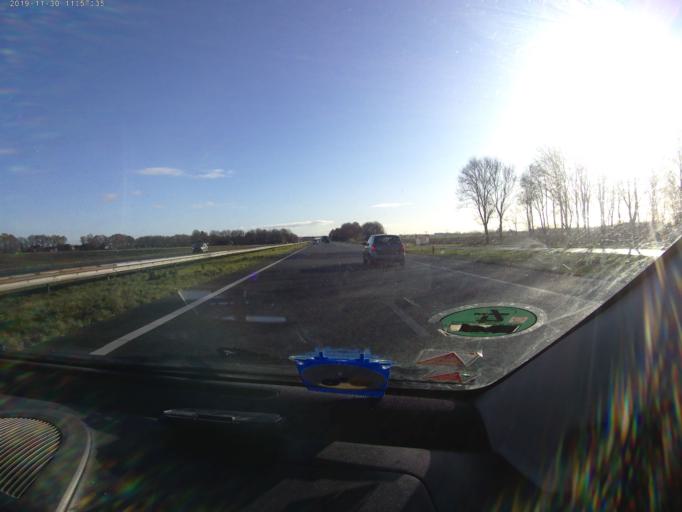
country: NL
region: Groningen
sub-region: Gemeente Hoogezand-Sappemeer
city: Hoogezand
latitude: 53.1926
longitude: 6.7049
